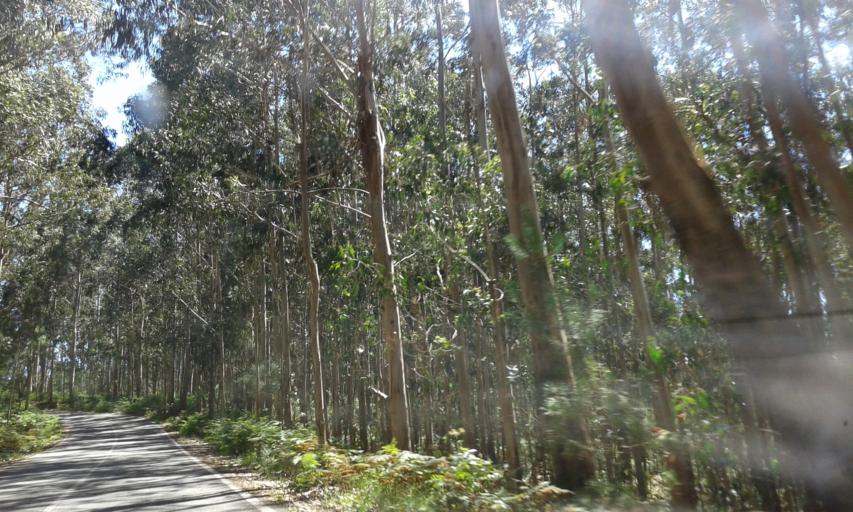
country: ES
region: Galicia
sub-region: Provincia de Pontevedra
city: Baiona
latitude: 42.1007
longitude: -8.8630
